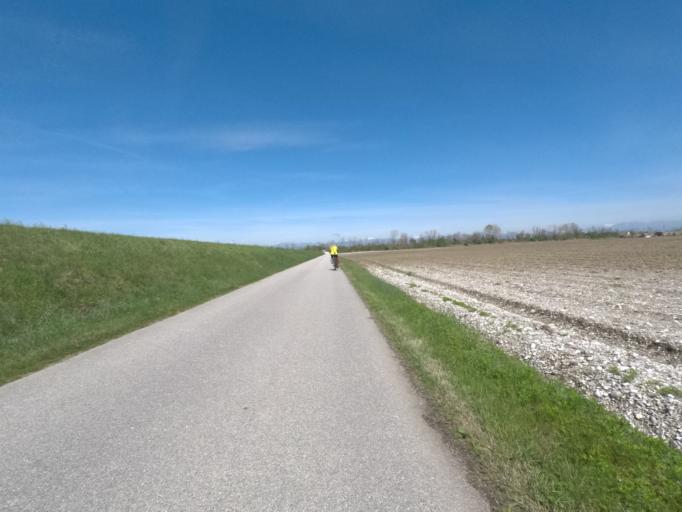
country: IT
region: Friuli Venezia Giulia
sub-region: Provincia di Udine
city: Camino al Tagliamento
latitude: 45.9560
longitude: 12.9135
